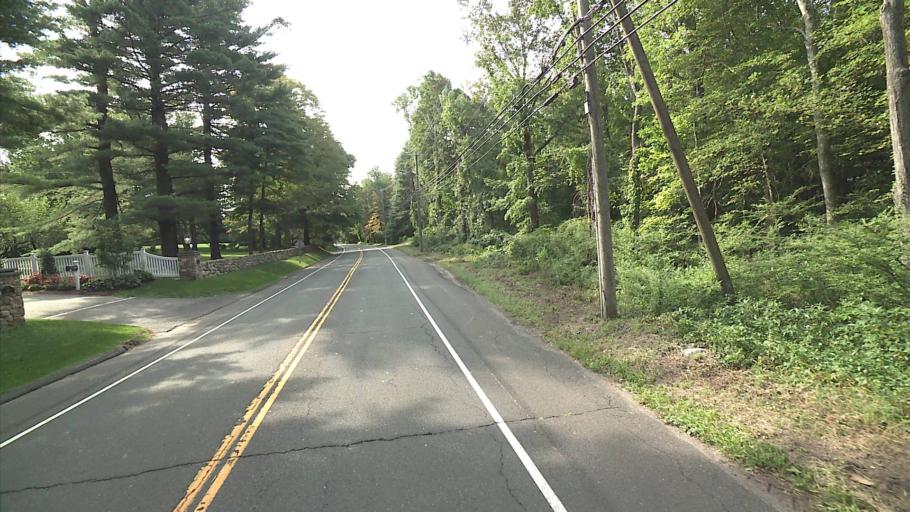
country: US
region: Connecticut
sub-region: Fairfield County
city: New Canaan
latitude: 41.1819
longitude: -73.5003
